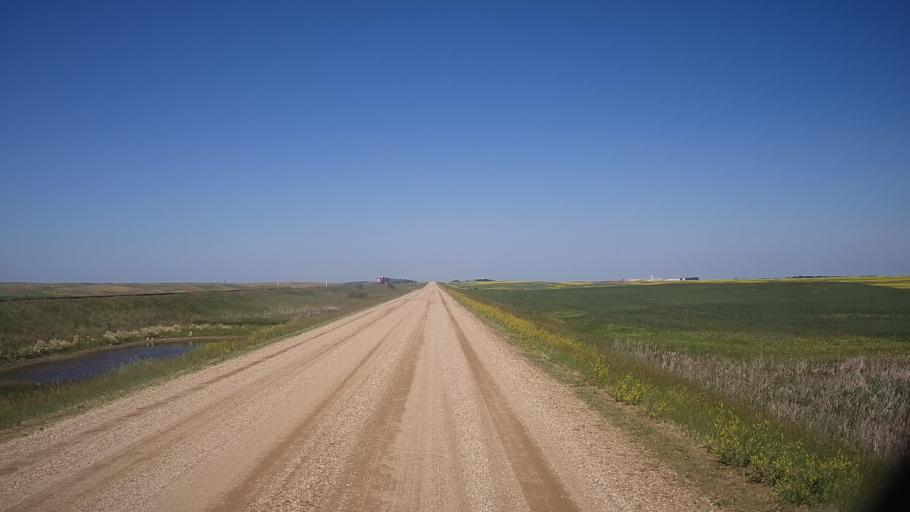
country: CA
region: Saskatchewan
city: Watrous
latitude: 51.8541
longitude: -105.9446
